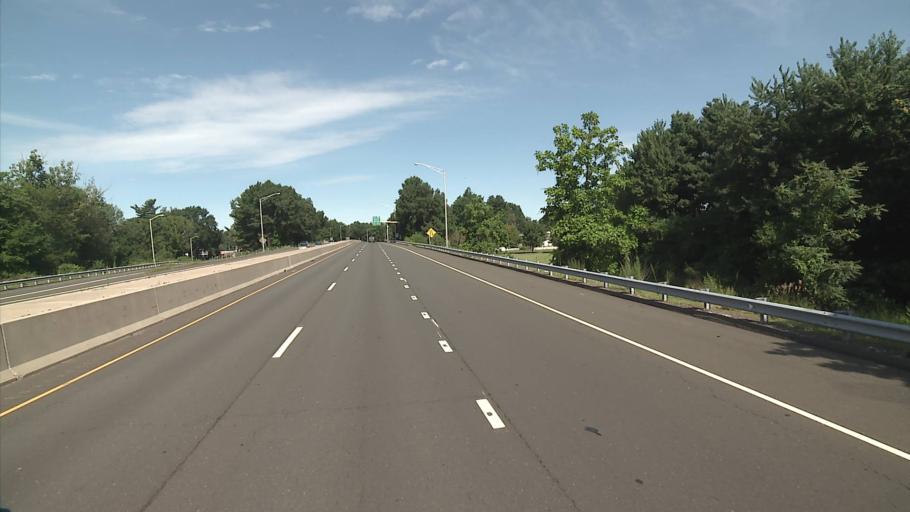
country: US
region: Connecticut
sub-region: Hartford County
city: Glastonbury
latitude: 41.7317
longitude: -72.6204
